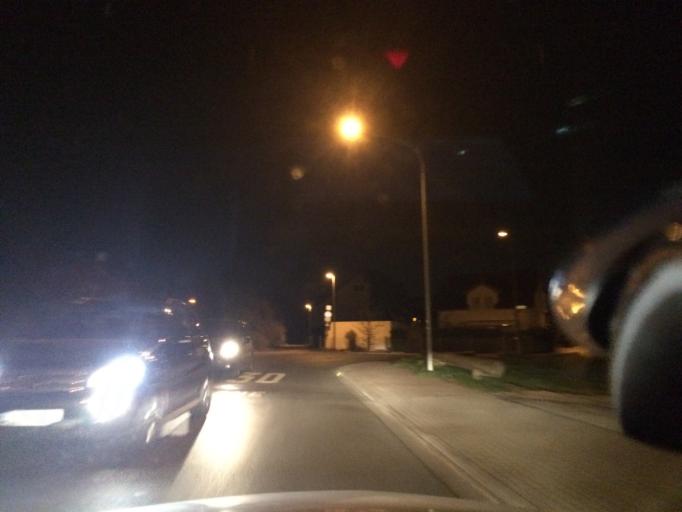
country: DE
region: Hesse
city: Griesheim
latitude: 49.8704
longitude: 8.5659
